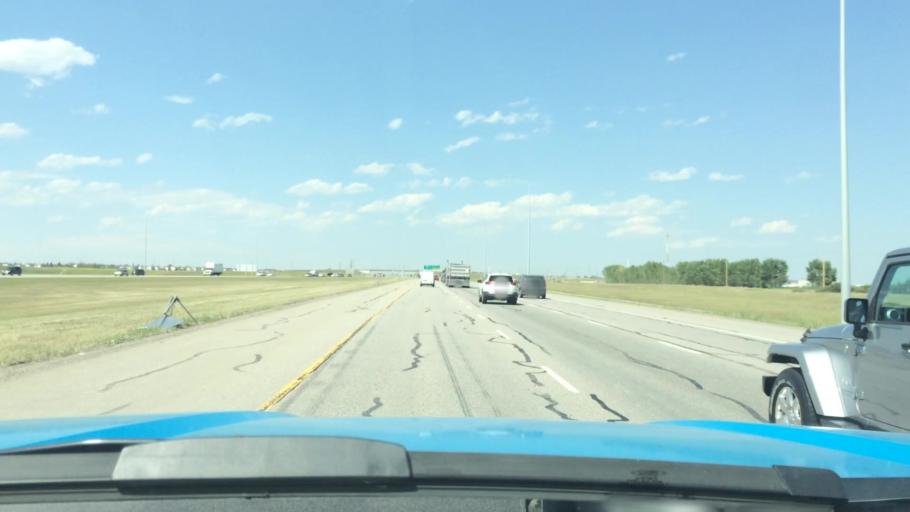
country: CA
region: Alberta
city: Chestermere
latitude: 51.0834
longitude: -113.9198
